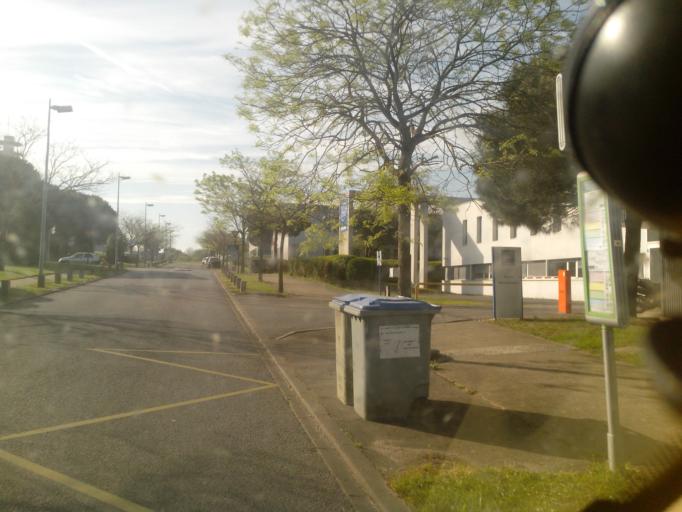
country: FR
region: Pays de la Loire
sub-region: Departement de la Loire-Atlantique
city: Saint-Herblain
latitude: 47.2267
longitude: -1.6206
